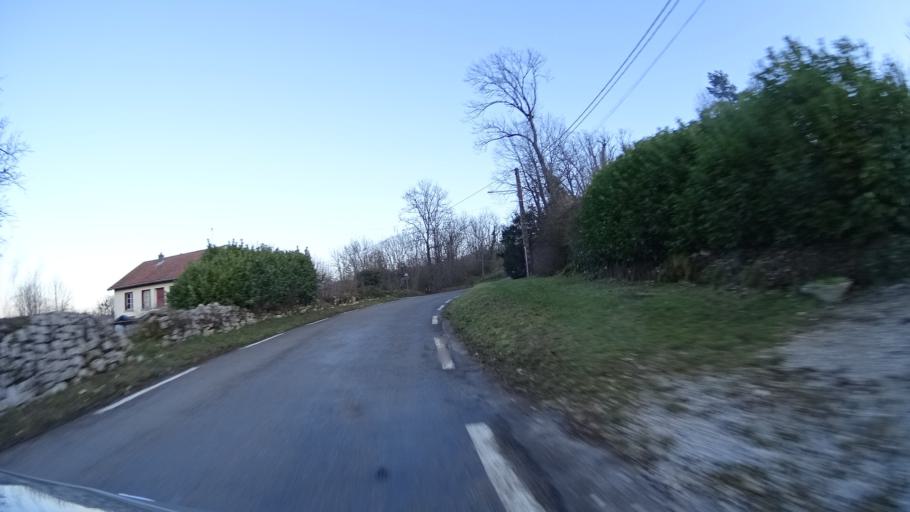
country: FR
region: Franche-Comte
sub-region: Departement du Doubs
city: Morre
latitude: 47.2231
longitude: 6.0412
